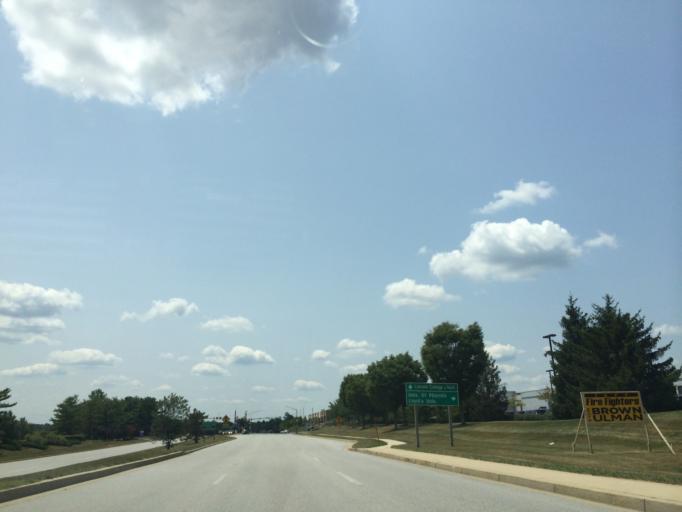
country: US
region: Maryland
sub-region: Howard County
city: Savage
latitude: 39.1876
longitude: -76.8156
